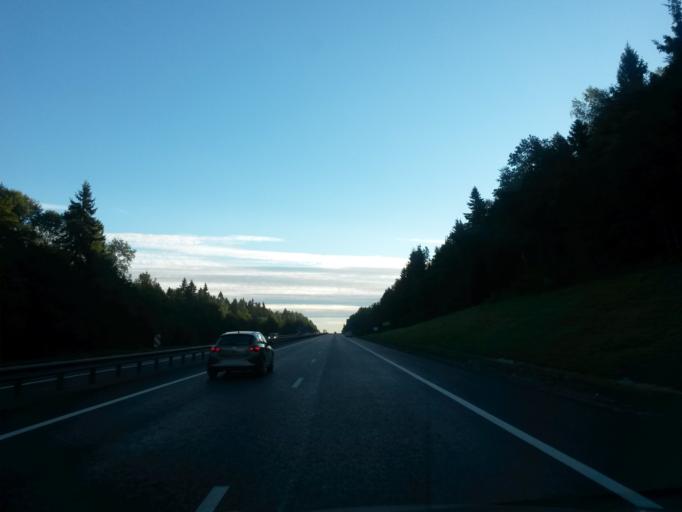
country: RU
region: Moskovskaya
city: Svatkovo
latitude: 56.3628
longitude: 38.2939
